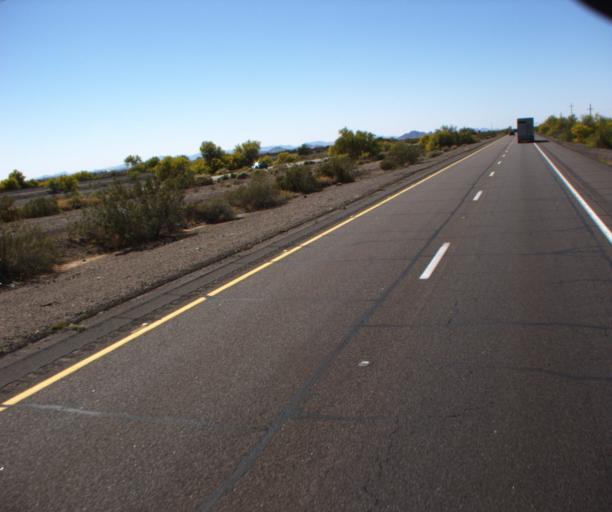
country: US
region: Arizona
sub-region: Maricopa County
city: Gila Bend
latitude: 32.8404
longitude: -113.3215
